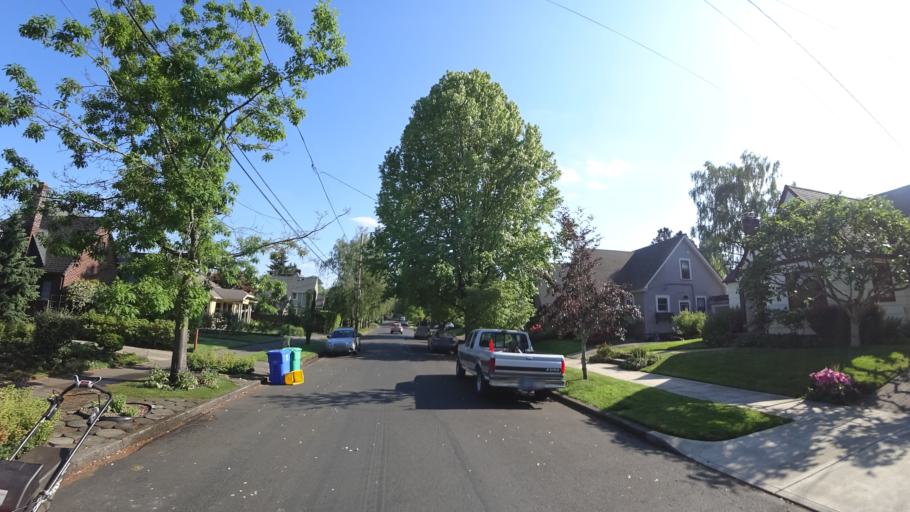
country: US
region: Oregon
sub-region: Multnomah County
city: Portland
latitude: 45.5460
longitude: -122.6381
